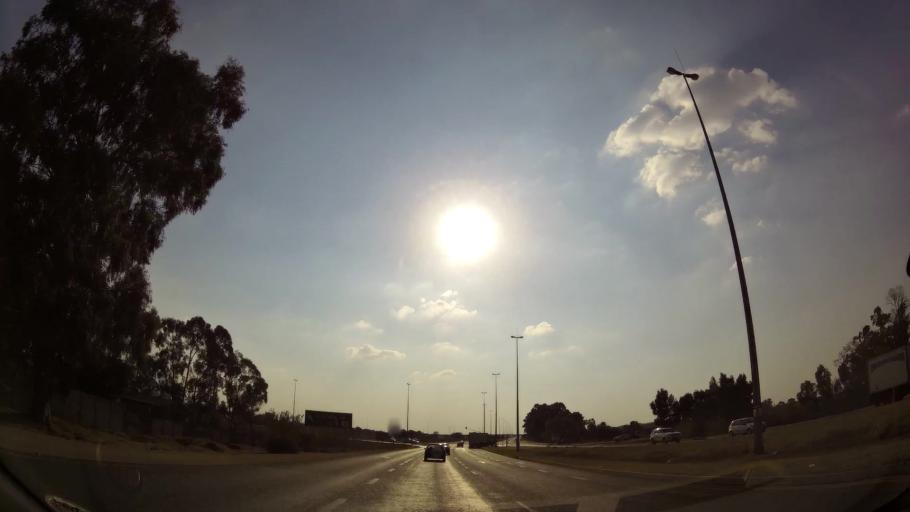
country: ZA
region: Gauteng
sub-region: Ekurhuleni Metropolitan Municipality
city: Benoni
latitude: -26.1110
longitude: 28.2618
